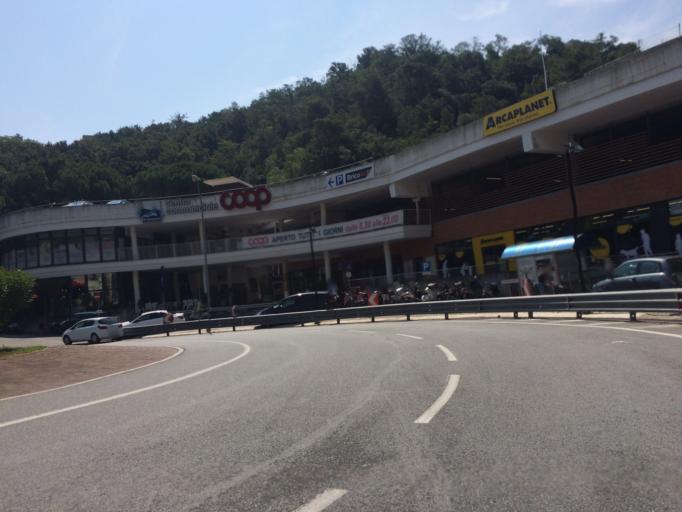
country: IT
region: Liguria
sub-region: Provincia di Genova
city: Arenzano
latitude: 44.4005
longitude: 8.6798
